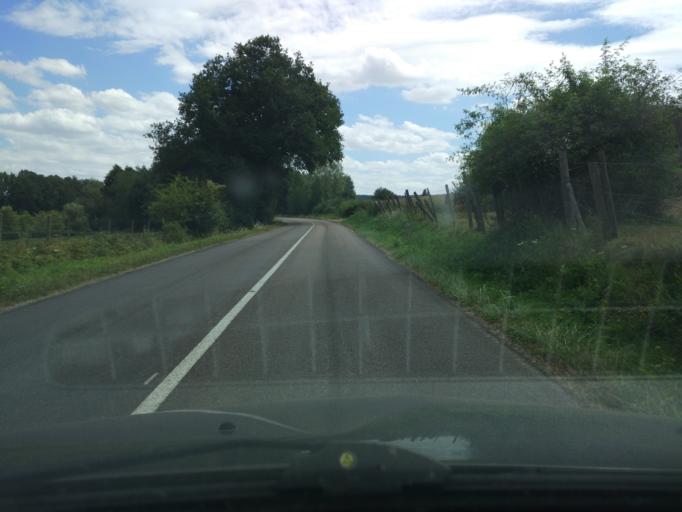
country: FR
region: Ile-de-France
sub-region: Departement de l'Essonne
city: Villiers-le-Bacle
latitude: 48.7135
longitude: 2.1188
